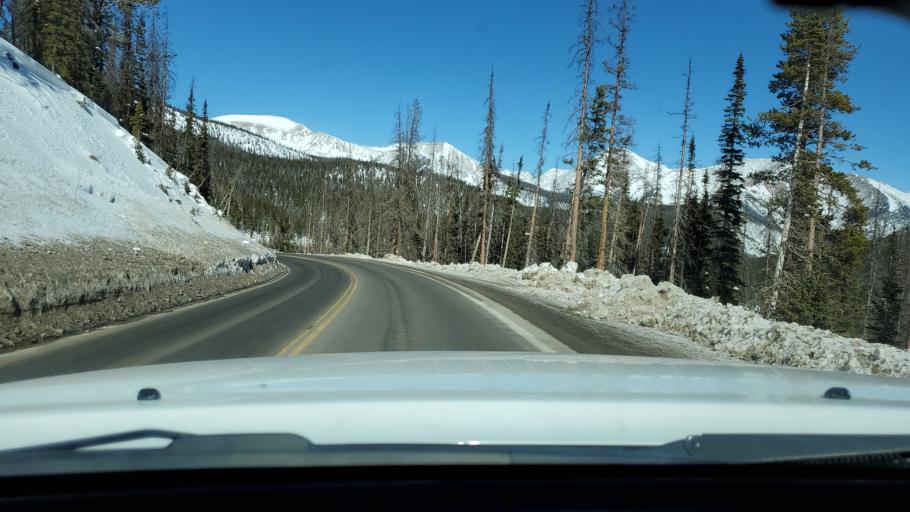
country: US
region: Colorado
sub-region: Chaffee County
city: Salida
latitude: 38.5088
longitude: -106.3261
